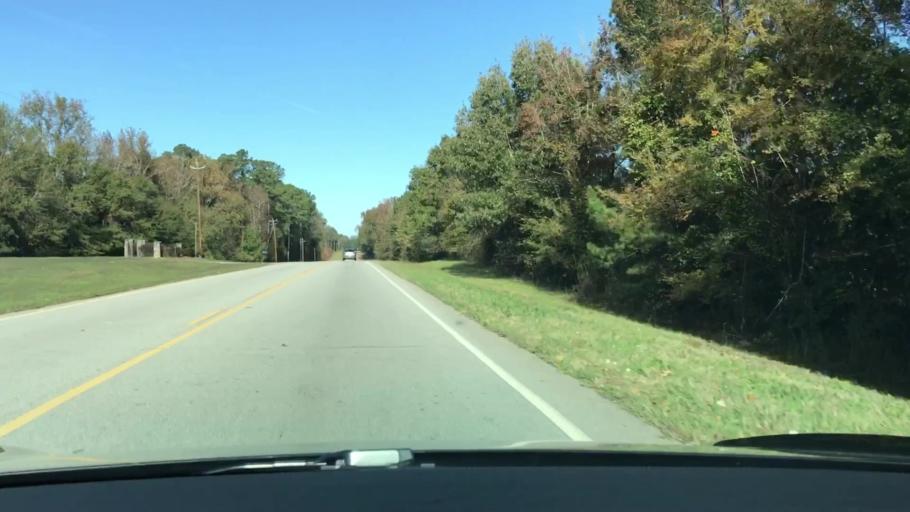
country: US
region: Georgia
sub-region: Warren County
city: Firing Range
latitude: 33.4288
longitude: -82.6846
